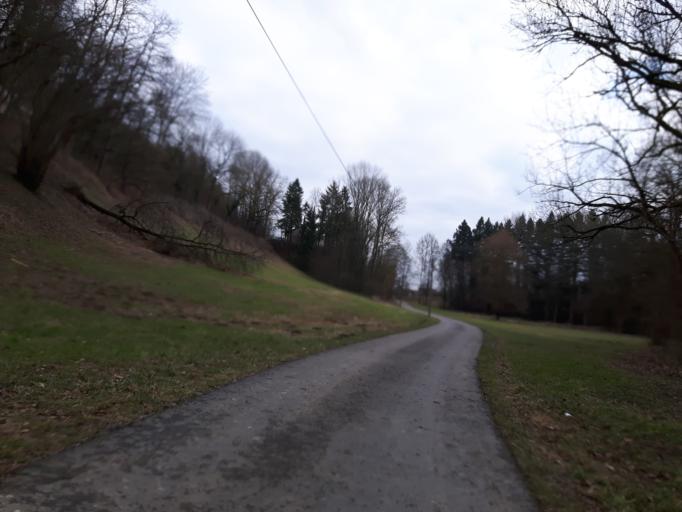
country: DE
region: Baden-Wuerttemberg
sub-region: Regierungsbezirk Stuttgart
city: Ohringen
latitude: 49.2136
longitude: 9.4701
